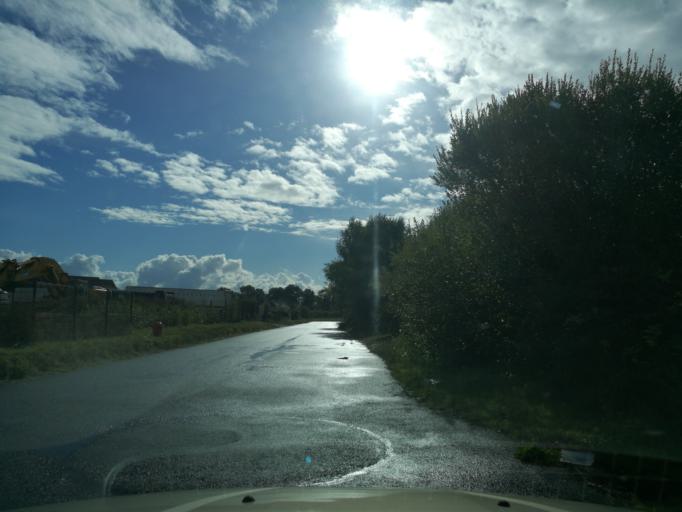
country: FR
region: Brittany
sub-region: Departement d'Ille-et-Vilaine
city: Pleumeleuc
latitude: 48.1841
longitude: -1.9291
